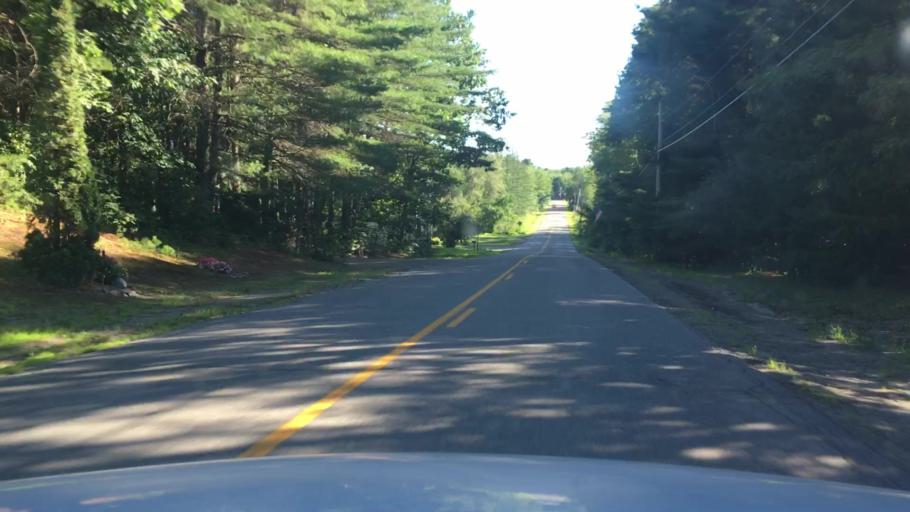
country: US
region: Maine
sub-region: Penobscot County
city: Enfield
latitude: 45.1899
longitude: -68.6099
